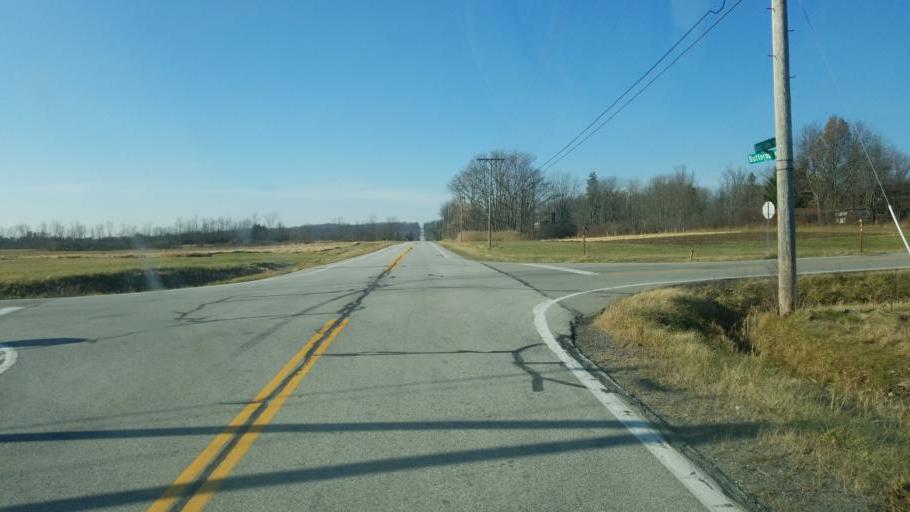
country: US
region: Ohio
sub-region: Geauga County
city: Burton
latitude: 41.4949
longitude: -81.2170
